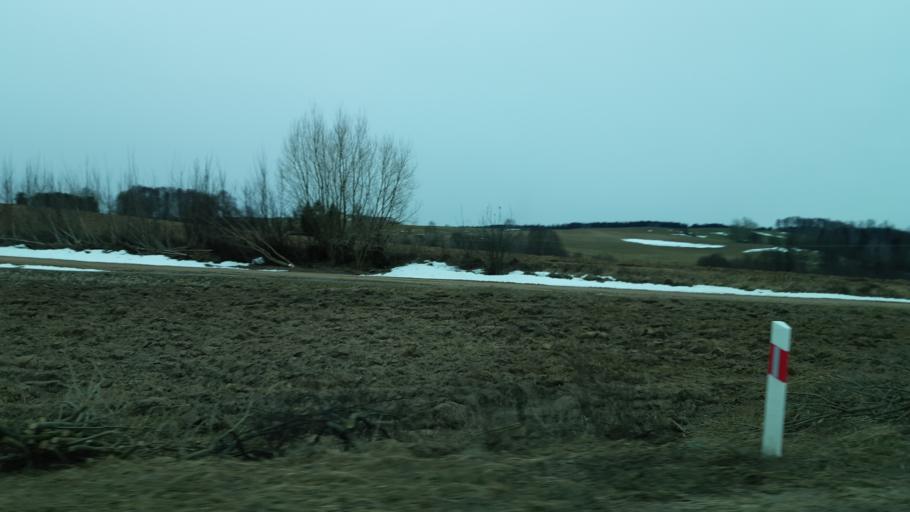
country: PL
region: Podlasie
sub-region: Suwalki
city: Suwalki
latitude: 54.3318
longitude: 22.9458
